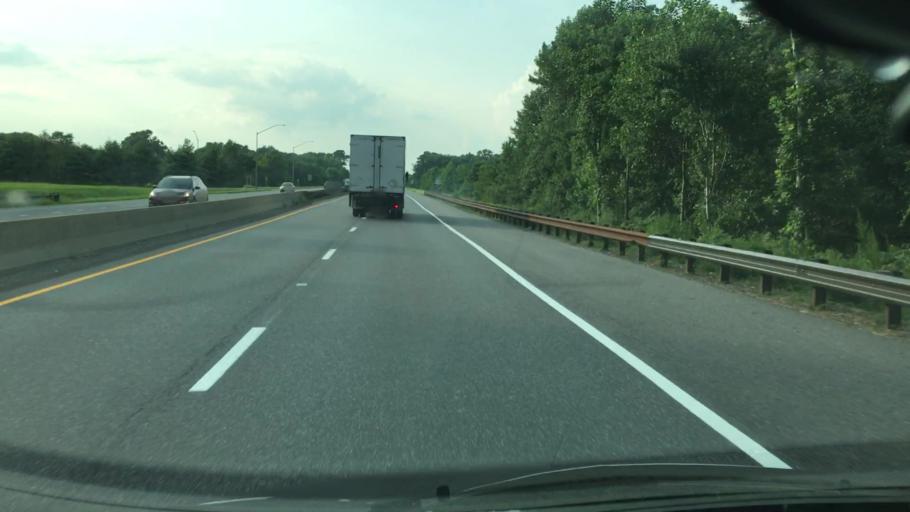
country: US
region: Maryland
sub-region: Worcester County
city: Ocean Pines
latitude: 38.3960
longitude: -75.2056
